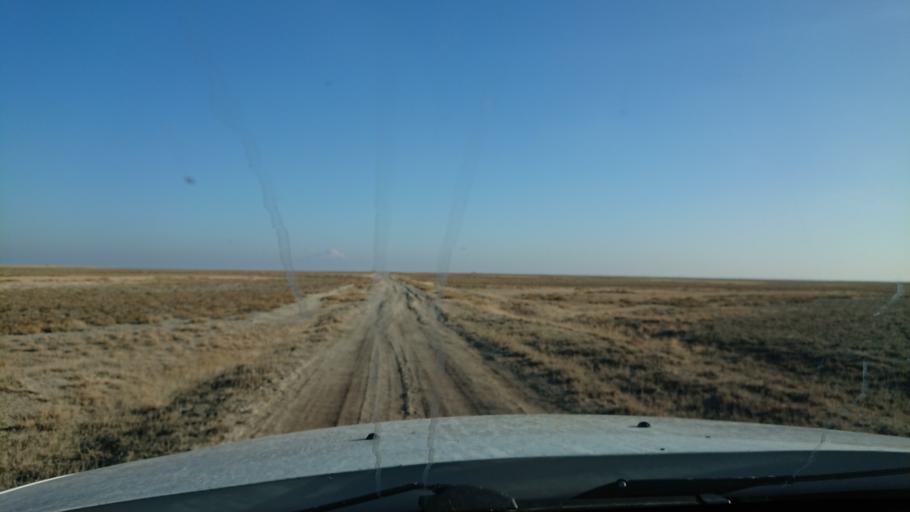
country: TR
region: Aksaray
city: Sultanhani
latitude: 38.4043
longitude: 33.5747
